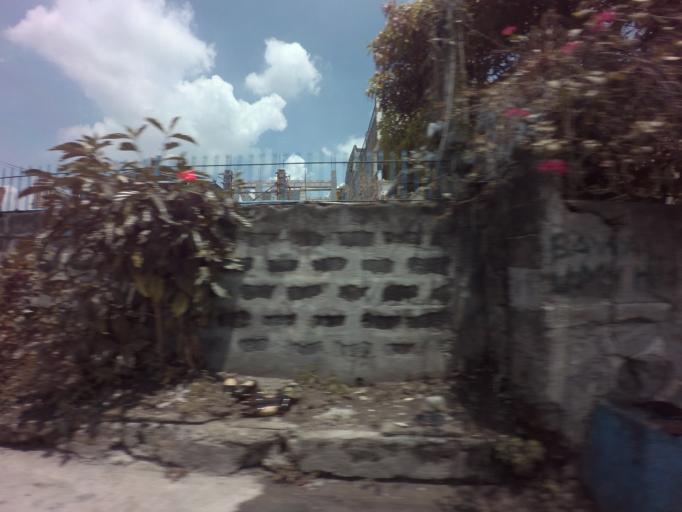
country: PH
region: Calabarzon
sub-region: Province of Laguna
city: San Pedro
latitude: 14.3916
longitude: 121.0506
